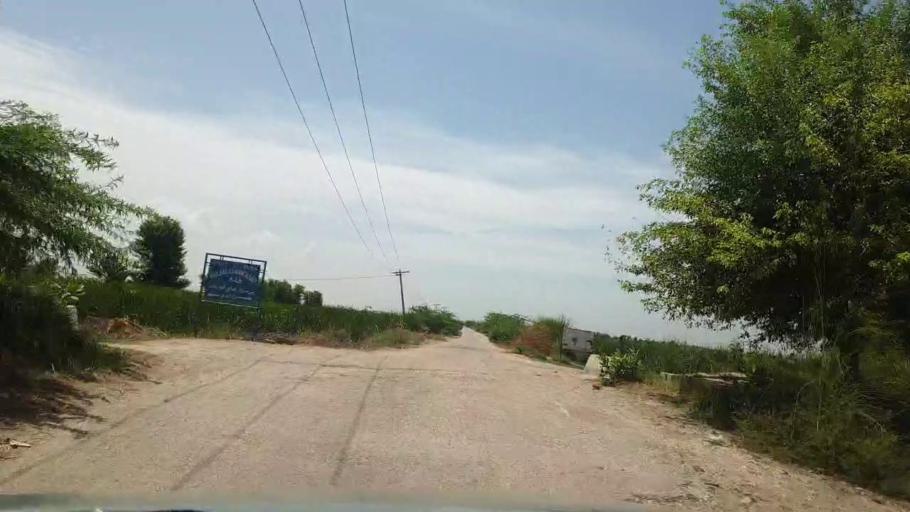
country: PK
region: Sindh
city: Bozdar
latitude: 27.0659
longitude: 68.9826
